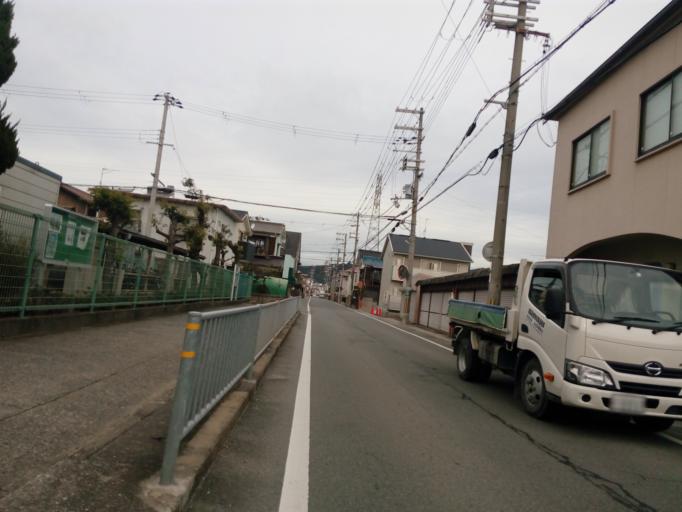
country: JP
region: Hyogo
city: Tatsunocho-tominaga
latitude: 34.7978
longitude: 134.6067
